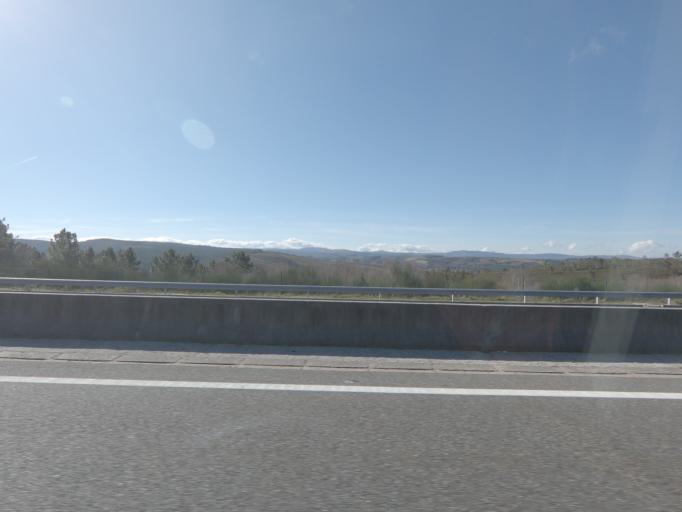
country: ES
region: Galicia
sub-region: Provincia de Pontevedra
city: Dozon
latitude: 42.5754
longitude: -8.0615
